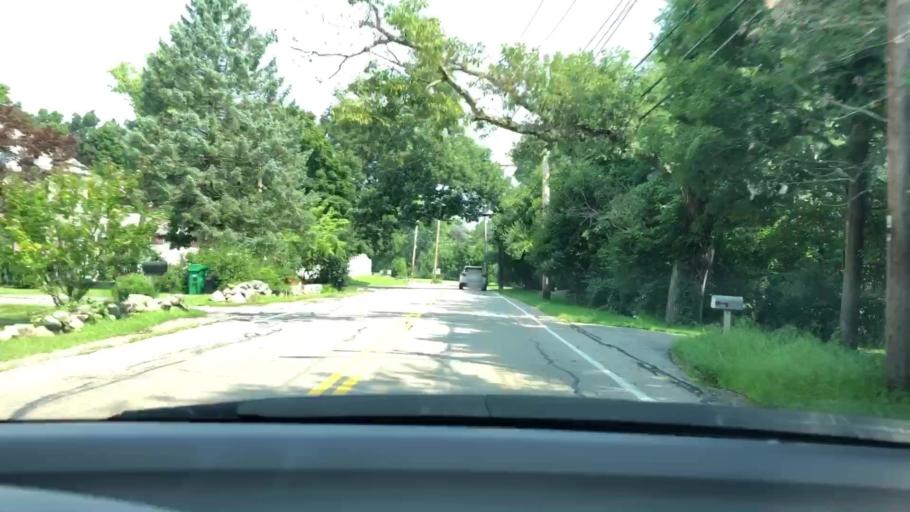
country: US
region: Massachusetts
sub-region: Norfolk County
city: Dedham
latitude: 42.2178
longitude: -71.1672
